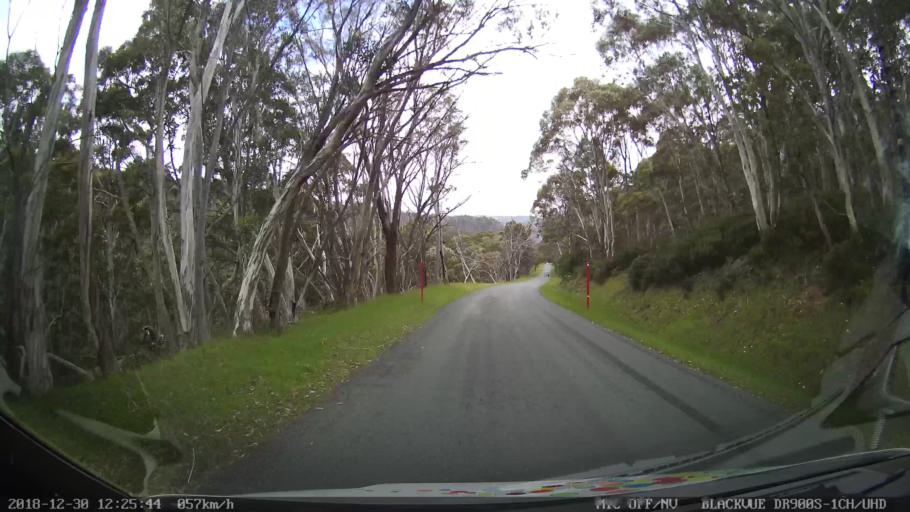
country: AU
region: New South Wales
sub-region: Snowy River
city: Jindabyne
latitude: -36.3466
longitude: 148.4887
